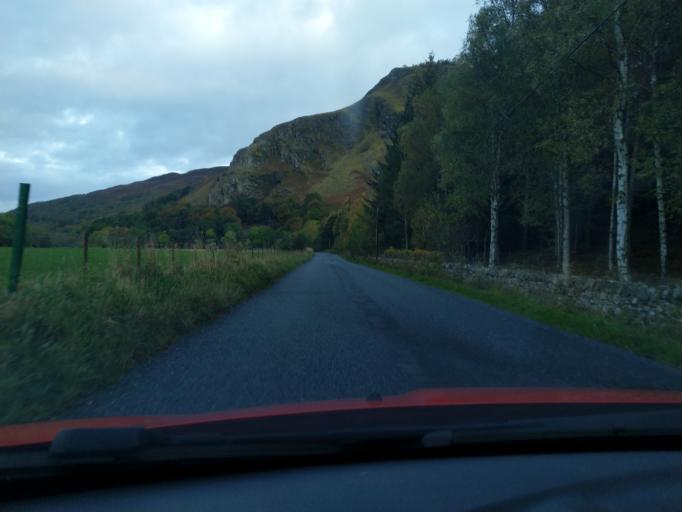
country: GB
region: Scotland
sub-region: Perth and Kinross
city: Aberfeldy
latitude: 56.6999
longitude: -4.1645
